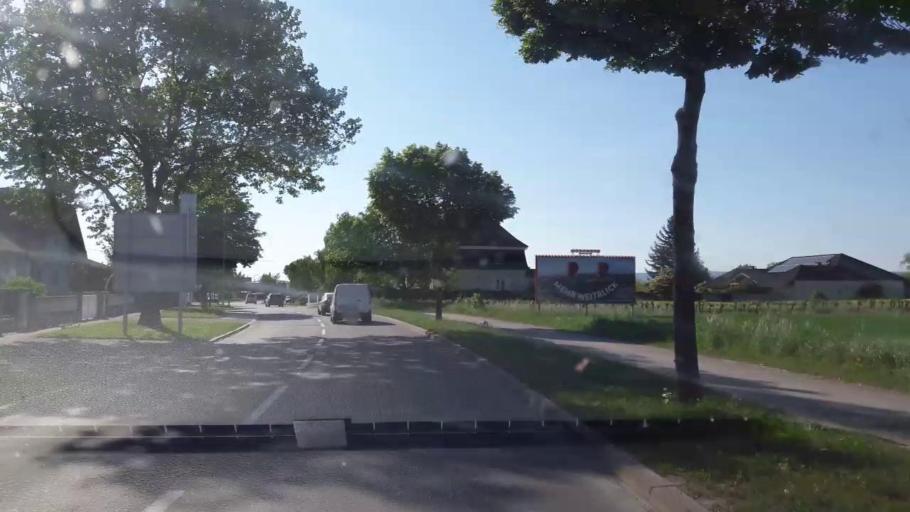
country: AT
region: Burgenland
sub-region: Eisenstadt-Umgebung
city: Sankt Margarethen im Burgenland
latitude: 47.8025
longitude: 16.6188
